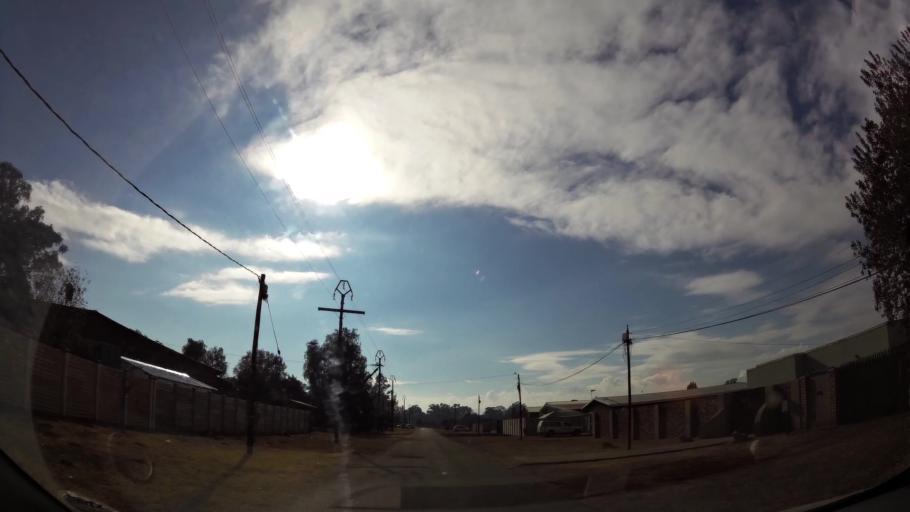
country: ZA
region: Gauteng
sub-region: Sedibeng District Municipality
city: Meyerton
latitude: -26.5505
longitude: 28.0584
